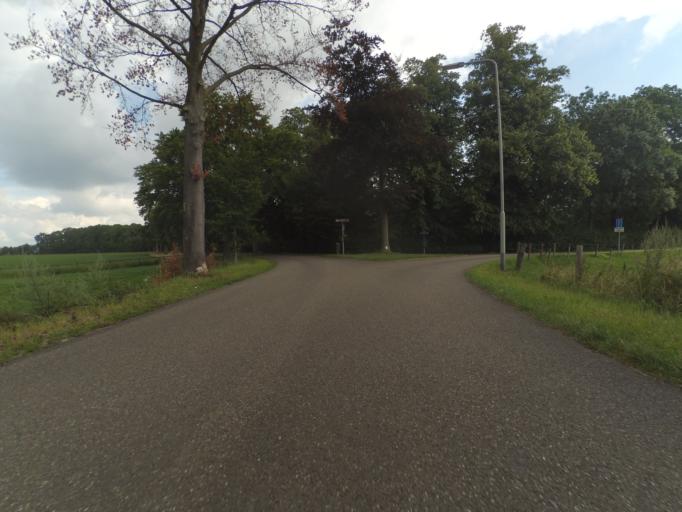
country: NL
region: Limburg
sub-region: Gemeente Maasgouw
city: Maasbracht
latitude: 51.1592
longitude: 5.9218
